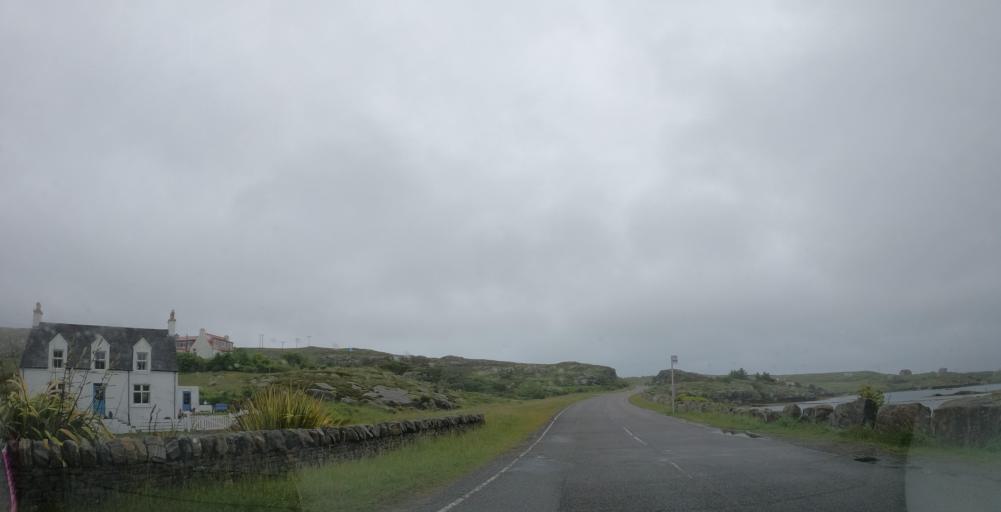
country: GB
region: Scotland
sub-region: Eilean Siar
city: Barra
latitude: 57.0020
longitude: -7.4304
